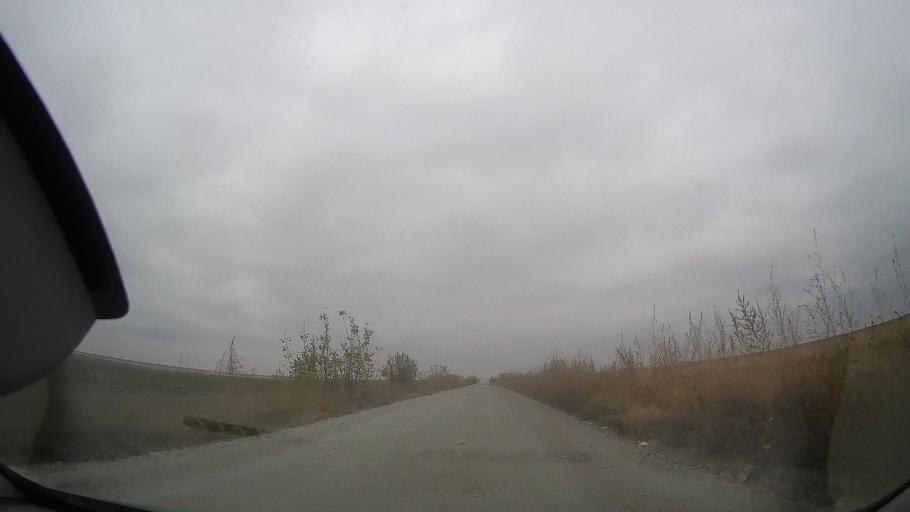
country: RO
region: Ialomita
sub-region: Comuna Grivita
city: Grivita
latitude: 44.7456
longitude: 27.2689
